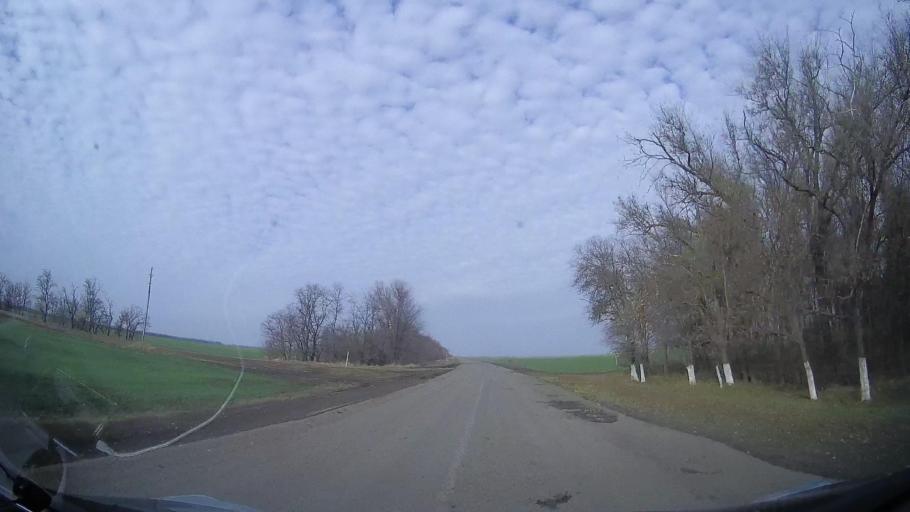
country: RU
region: Rostov
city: Gigant
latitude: 46.9284
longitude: 41.2458
